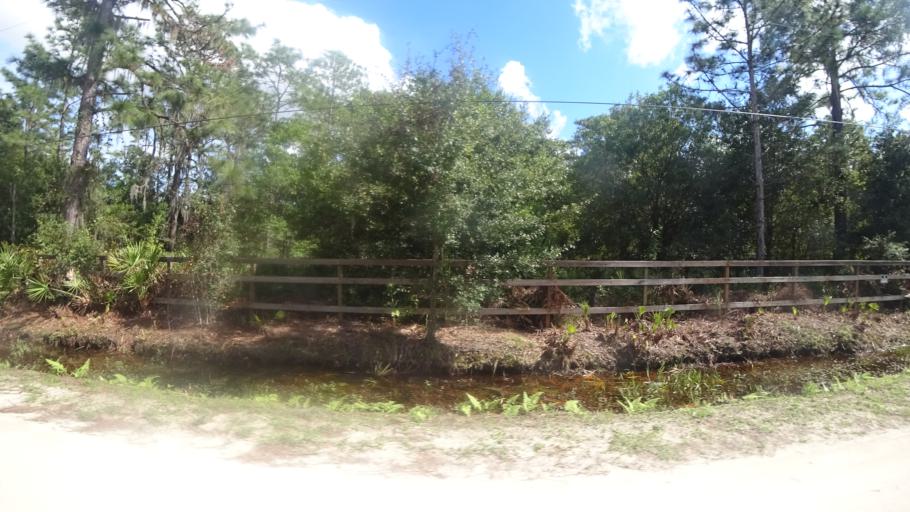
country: US
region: Florida
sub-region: Hillsborough County
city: Sun City Center
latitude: 27.6390
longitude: -82.3611
